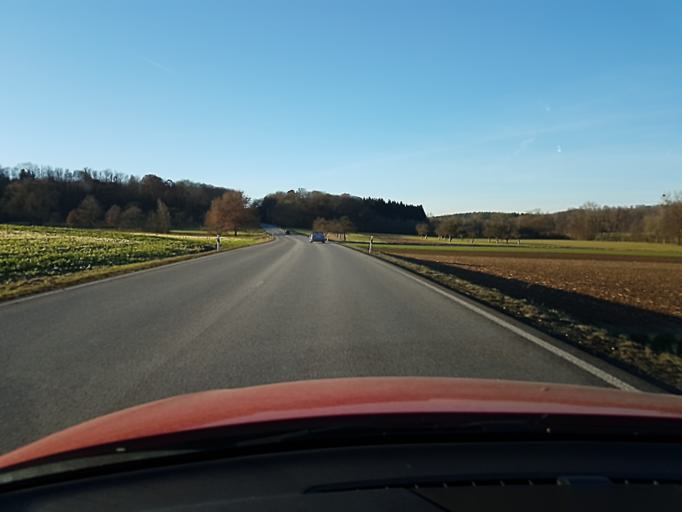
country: DE
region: Baden-Wuerttemberg
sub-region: Karlsruhe Region
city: Illingen
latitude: 48.9630
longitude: 8.8948
